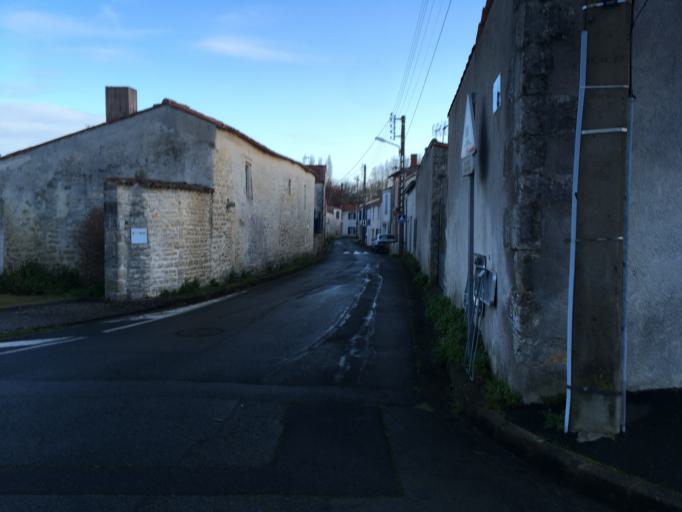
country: FR
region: Poitou-Charentes
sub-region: Departement de la Charente-Maritime
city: Nieul-sur-Mer
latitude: 46.2060
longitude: -1.1662
